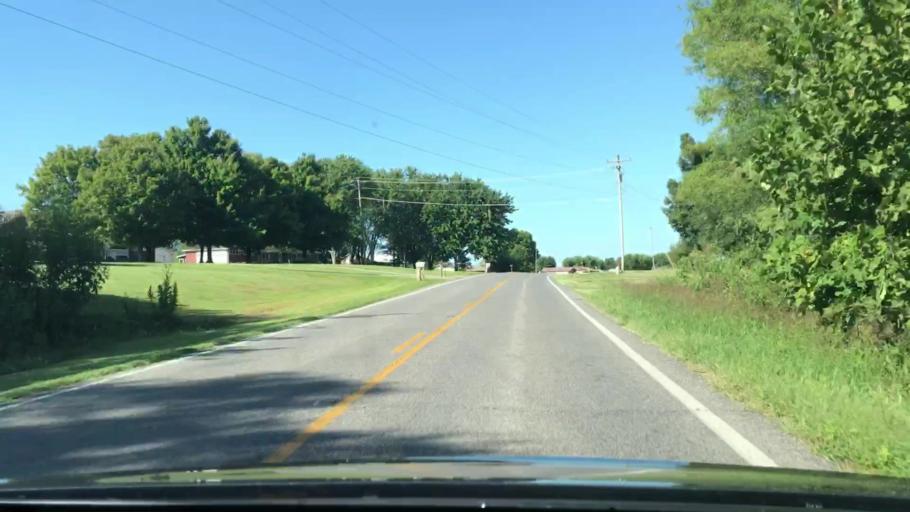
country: US
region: Kentucky
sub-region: Graves County
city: Mayfield
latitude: 36.7621
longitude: -88.5819
